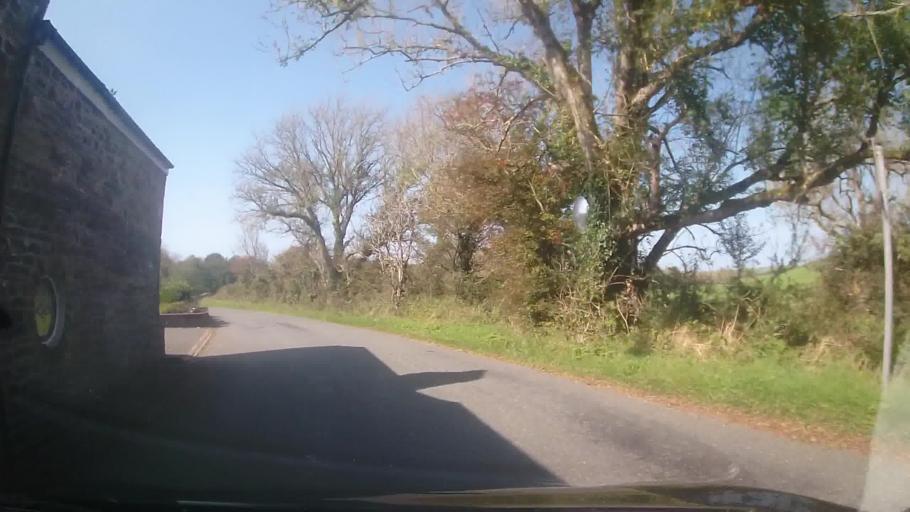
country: GB
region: Wales
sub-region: Pembrokeshire
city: Camrose
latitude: 51.8389
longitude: -4.9830
